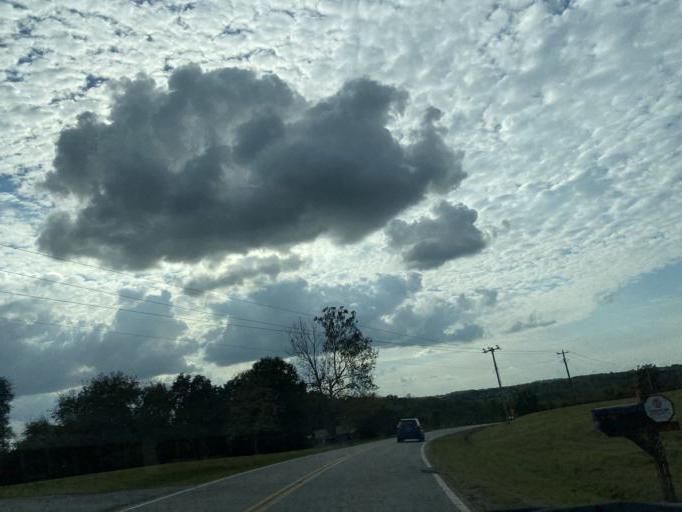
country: US
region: South Carolina
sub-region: Cherokee County
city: Gaffney
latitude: 35.0714
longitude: -81.7173
